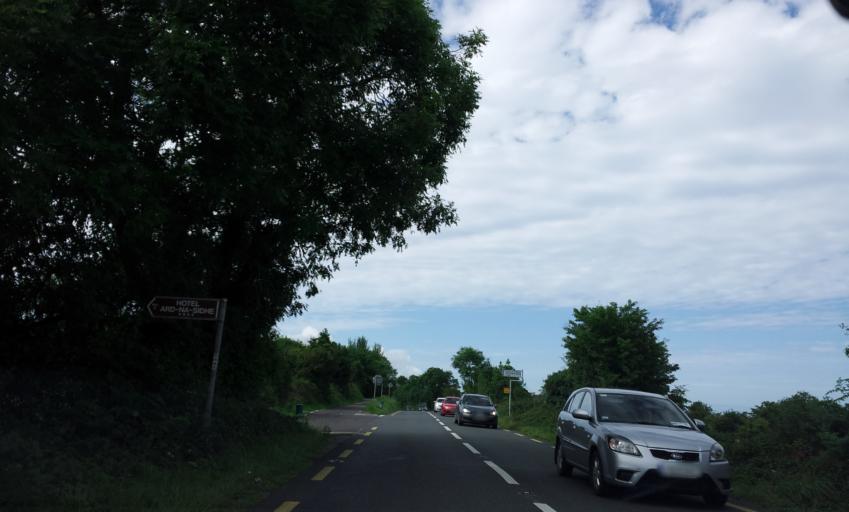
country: IE
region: Munster
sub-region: Ciarrai
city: Killorglin
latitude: 52.0865
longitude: -9.8576
